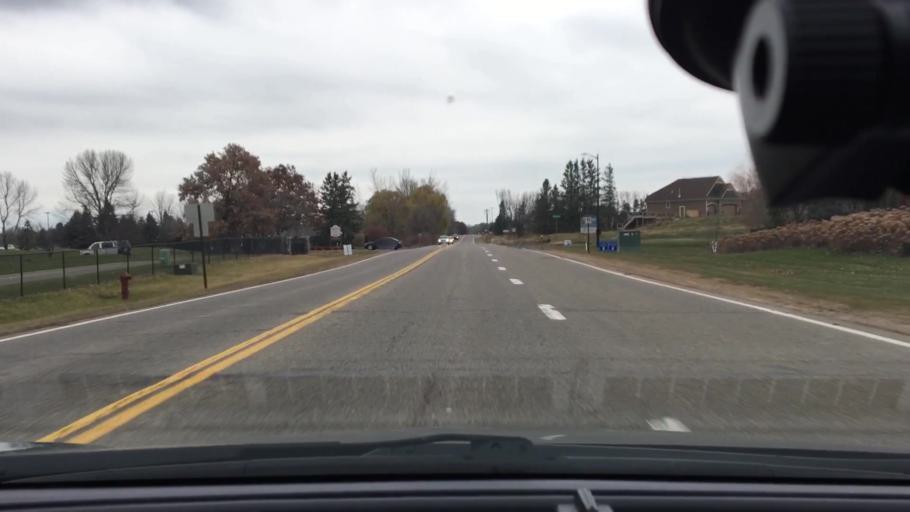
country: US
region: Minnesota
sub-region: Hennepin County
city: Corcoran
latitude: 45.0958
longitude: -93.5124
